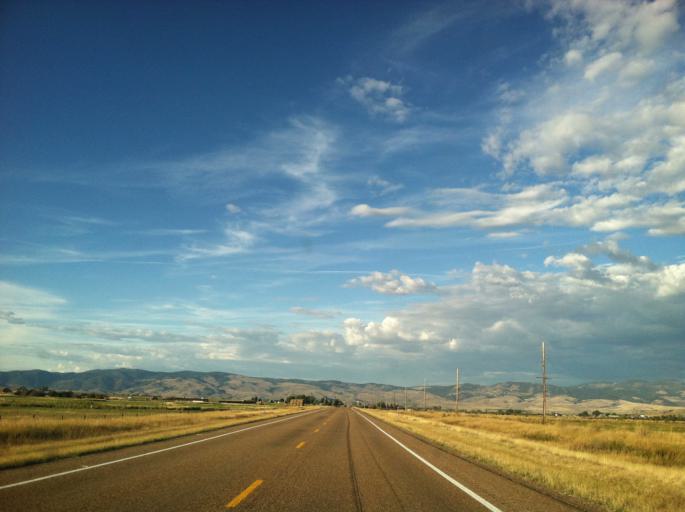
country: US
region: Montana
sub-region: Granite County
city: Philipsburg
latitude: 46.5696
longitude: -113.2072
